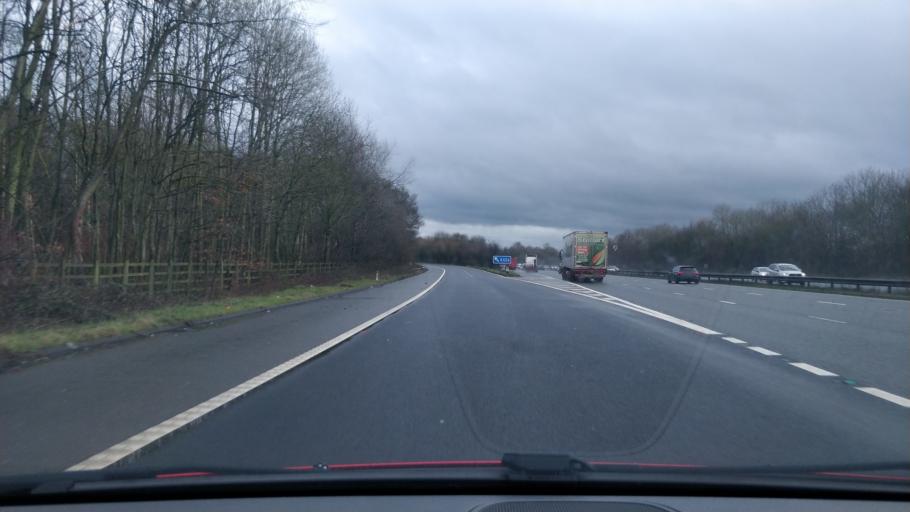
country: GB
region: England
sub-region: Knowsley
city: Knowsley
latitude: 53.4393
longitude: -2.8569
